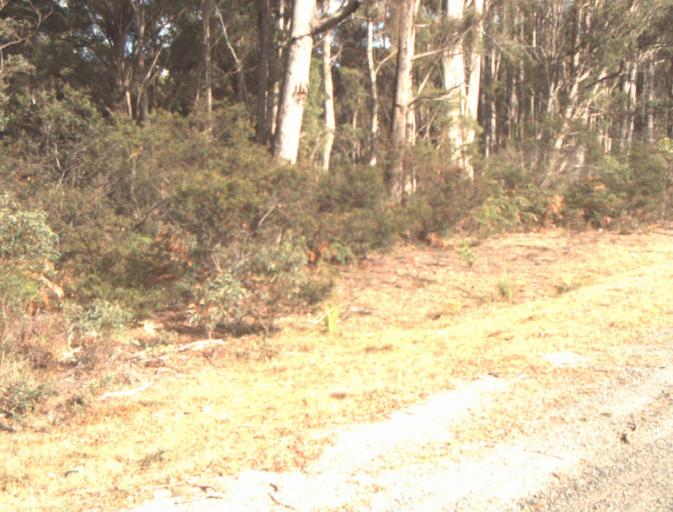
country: AU
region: Tasmania
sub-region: Dorset
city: Bridport
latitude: -41.1694
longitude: 147.2629
